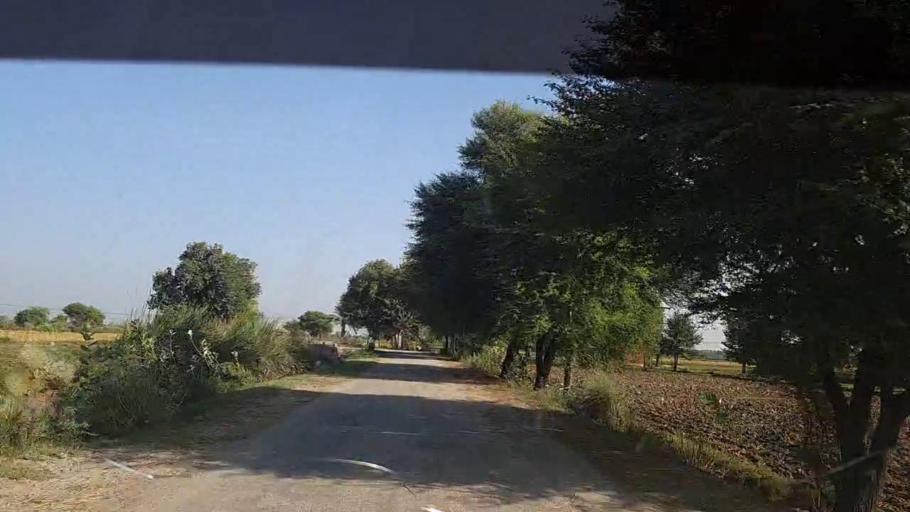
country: PK
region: Sindh
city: Larkana
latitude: 27.6221
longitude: 68.2440
